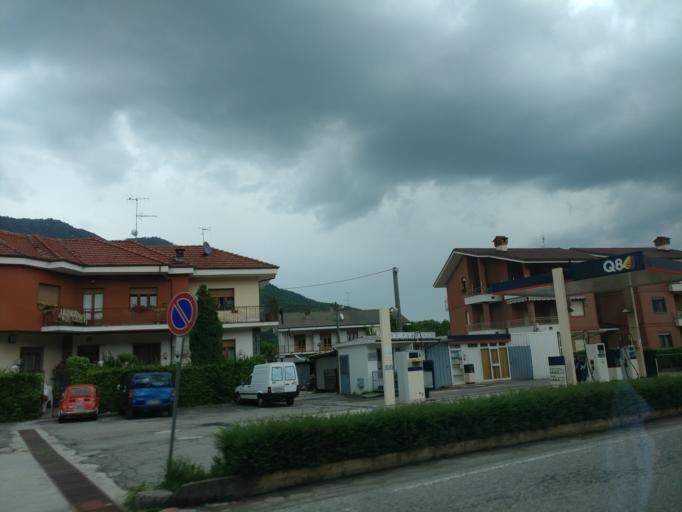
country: IT
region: Piedmont
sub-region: Provincia di Cuneo
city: Sanfront
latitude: 44.6481
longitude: 7.3215
